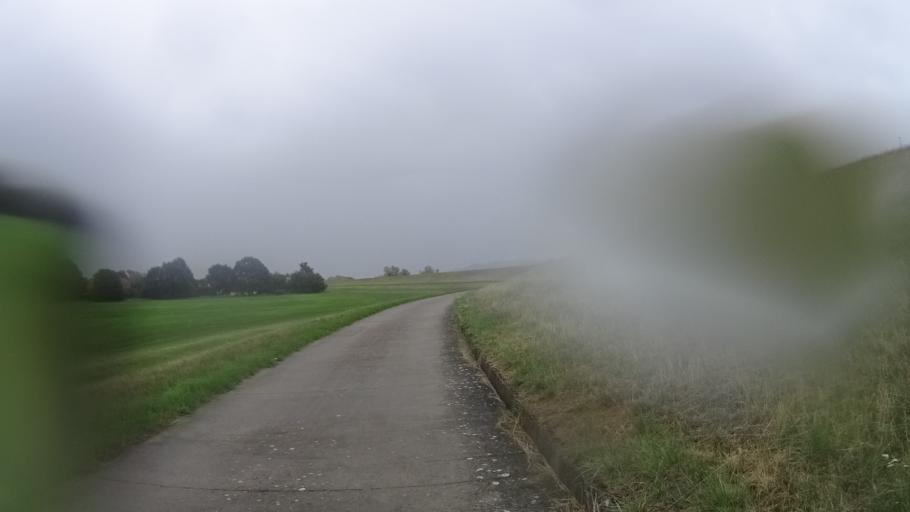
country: DE
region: Lower Saxony
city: Hitzacker
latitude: 53.1863
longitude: 11.0096
